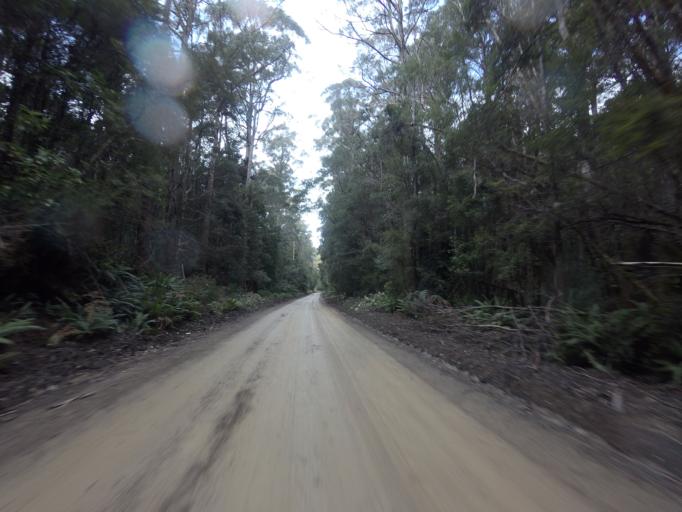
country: AU
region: Tasmania
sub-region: Huon Valley
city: Geeveston
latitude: -43.3879
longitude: 146.8498
